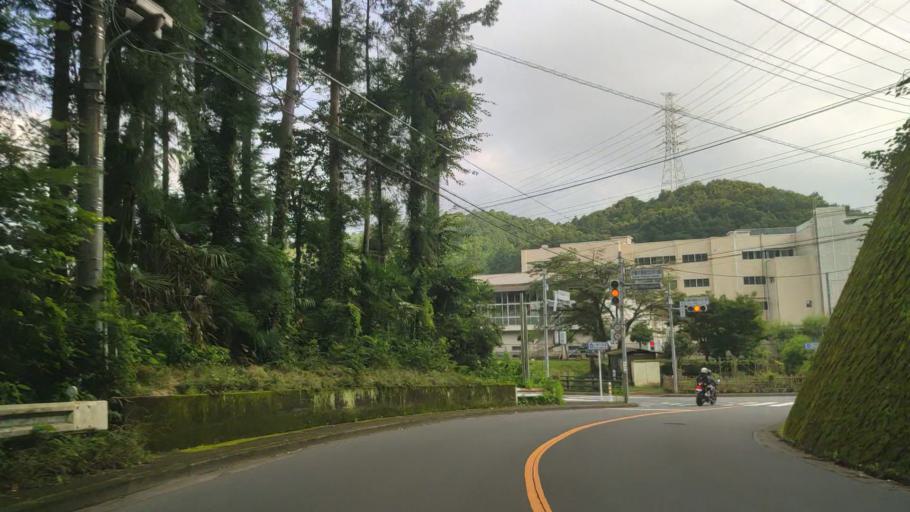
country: JP
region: Saitama
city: Hanno
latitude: 35.8226
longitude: 139.2767
